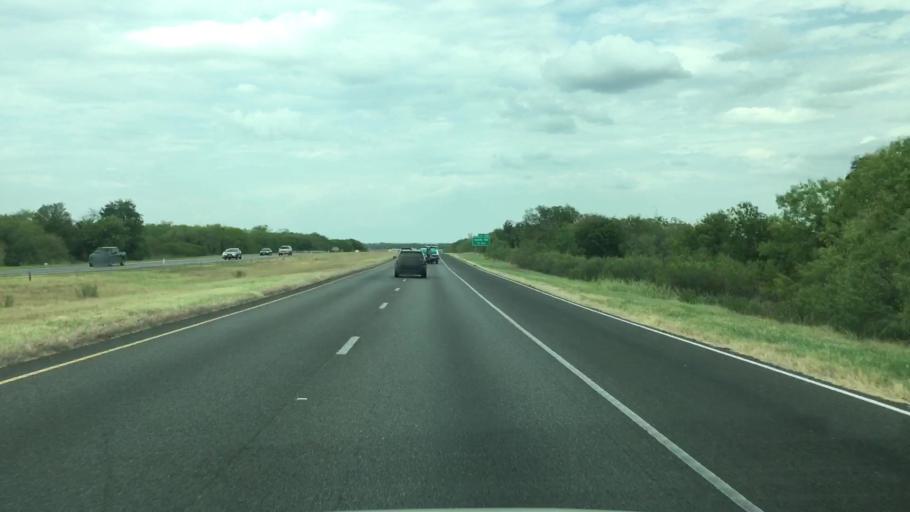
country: US
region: Texas
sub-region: Bexar County
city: Elmendorf
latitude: 29.1299
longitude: -98.4301
